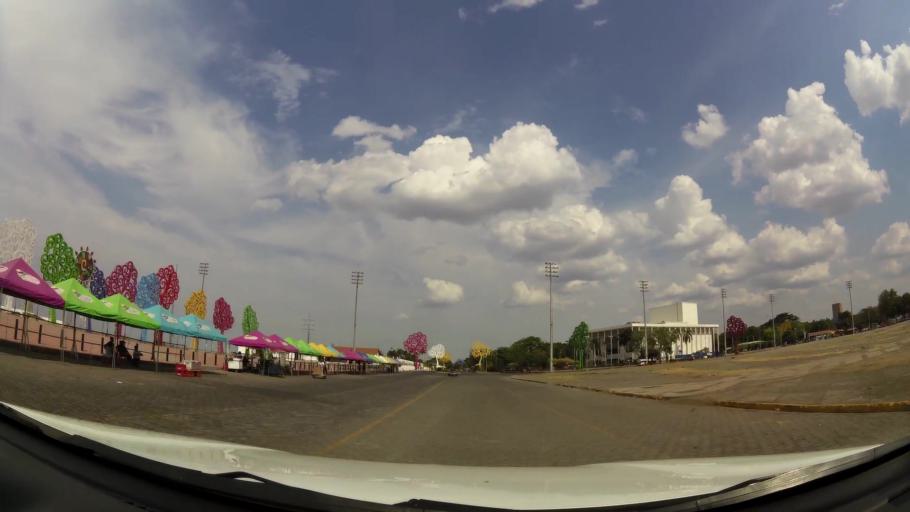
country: NI
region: Managua
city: Managua
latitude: 12.1603
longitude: -86.2740
